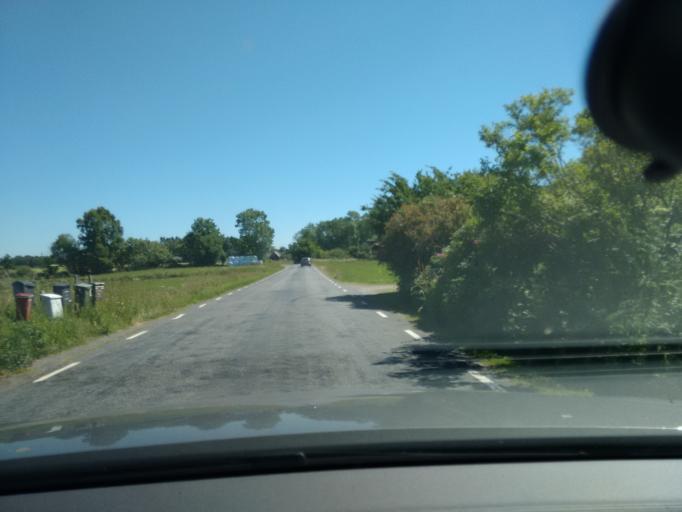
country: SE
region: Skane
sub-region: Kristianstads Kommun
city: Degeberga
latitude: 55.7794
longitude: 14.0867
